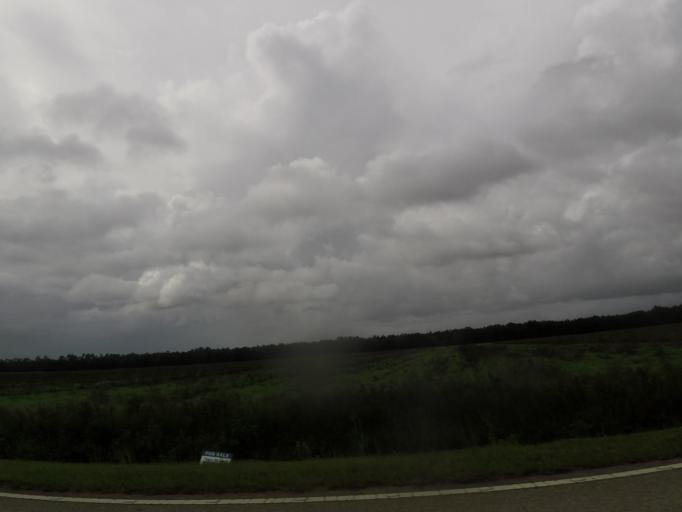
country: US
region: Florida
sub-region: Saint Johns County
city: Saint Augustine South
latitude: 29.8517
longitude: -81.4885
